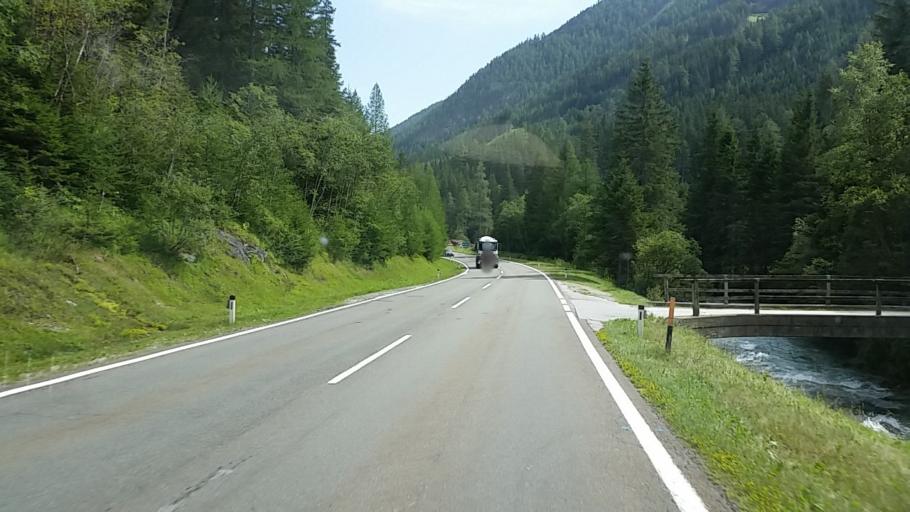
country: AT
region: Salzburg
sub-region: Politischer Bezirk Tamsweg
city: Mauterndorf
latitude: 47.1481
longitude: 13.6569
